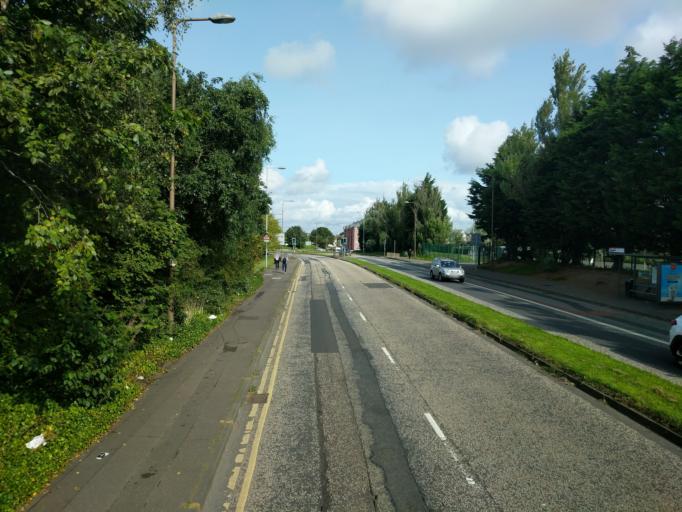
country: GB
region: Scotland
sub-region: Edinburgh
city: Currie
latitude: 55.9308
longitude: -3.2927
